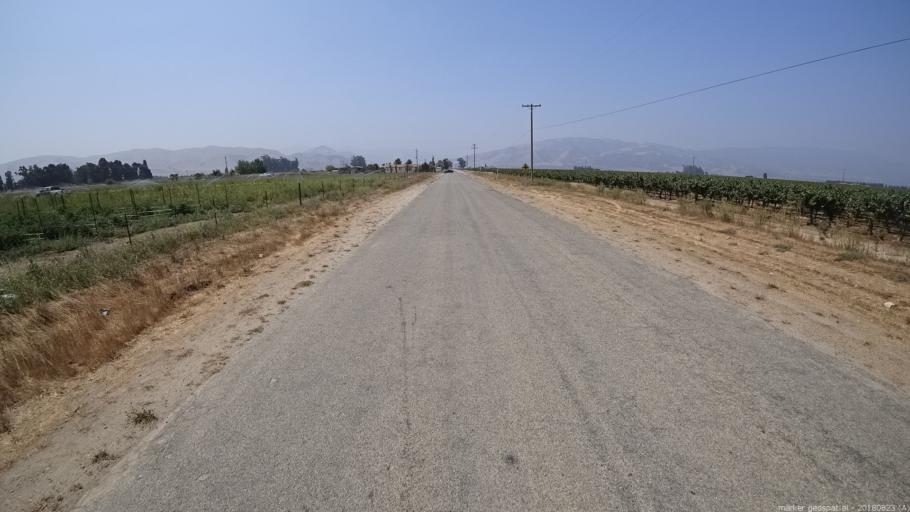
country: US
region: California
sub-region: Monterey County
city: Greenfield
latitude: 36.3194
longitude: -121.2617
